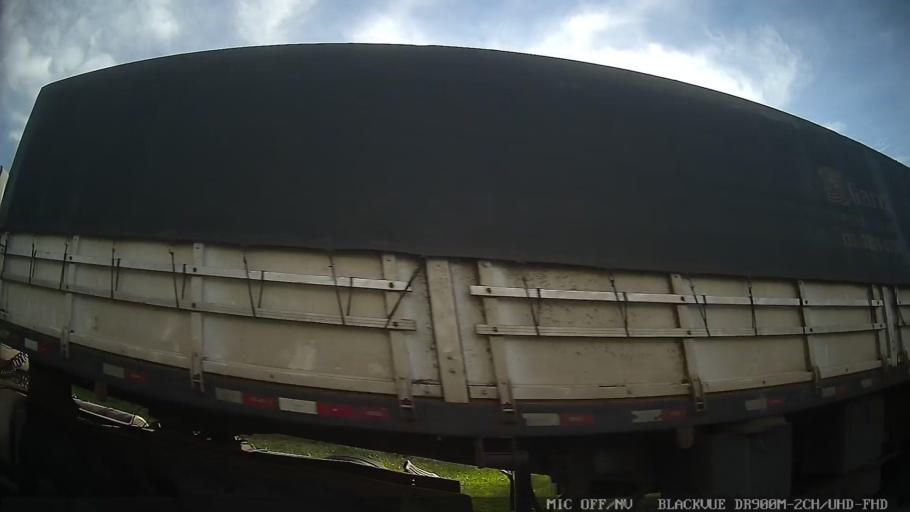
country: BR
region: Sao Paulo
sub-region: Tiete
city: Tiete
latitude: -23.1716
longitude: -47.6429
